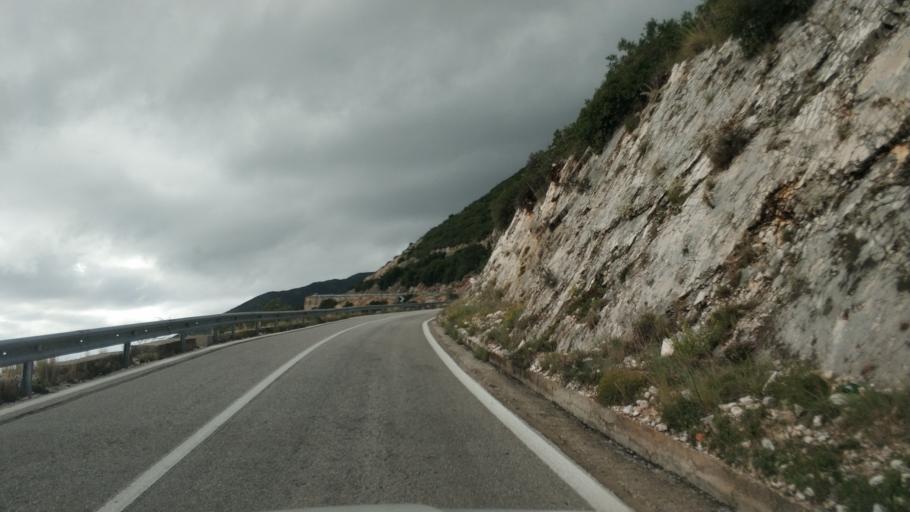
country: AL
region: Vlore
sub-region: Rrethi i Vlores
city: Vranisht
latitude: 40.1791
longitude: 19.5950
